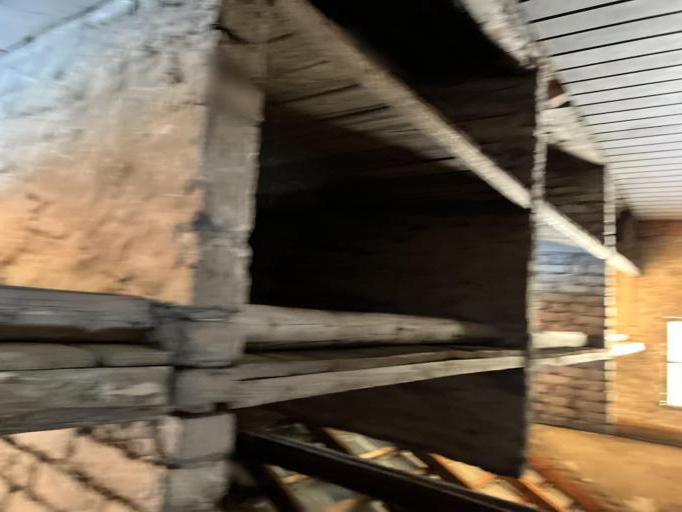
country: PL
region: Lesser Poland Voivodeship
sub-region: Powiat oswiecimski
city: Brzezinka
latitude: 50.0325
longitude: 19.1798
